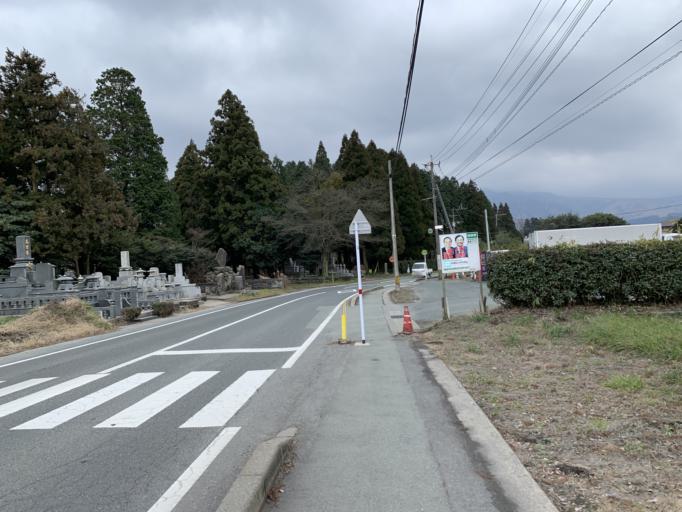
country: JP
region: Kumamoto
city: Aso
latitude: 32.9371
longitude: 131.1141
